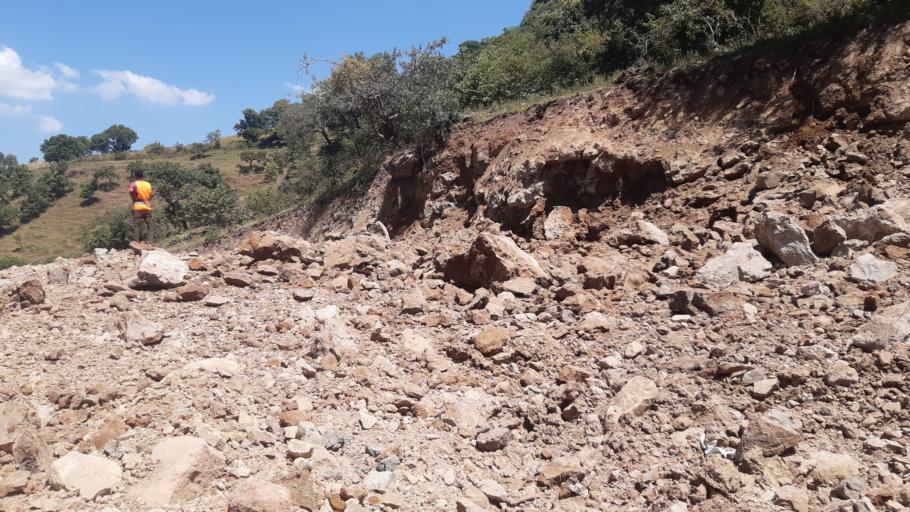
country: ET
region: Amhara
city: Dabat
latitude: 13.1768
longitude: 37.5974
